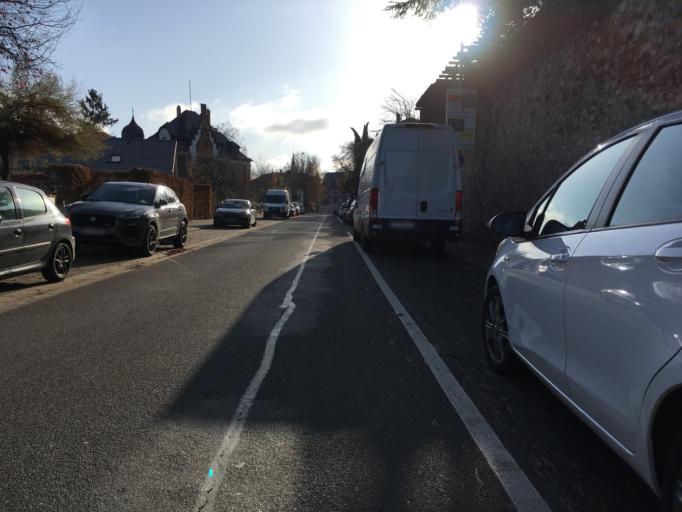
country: DE
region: Rheinland-Pfalz
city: Bodenheim
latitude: 49.9322
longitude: 8.3048
